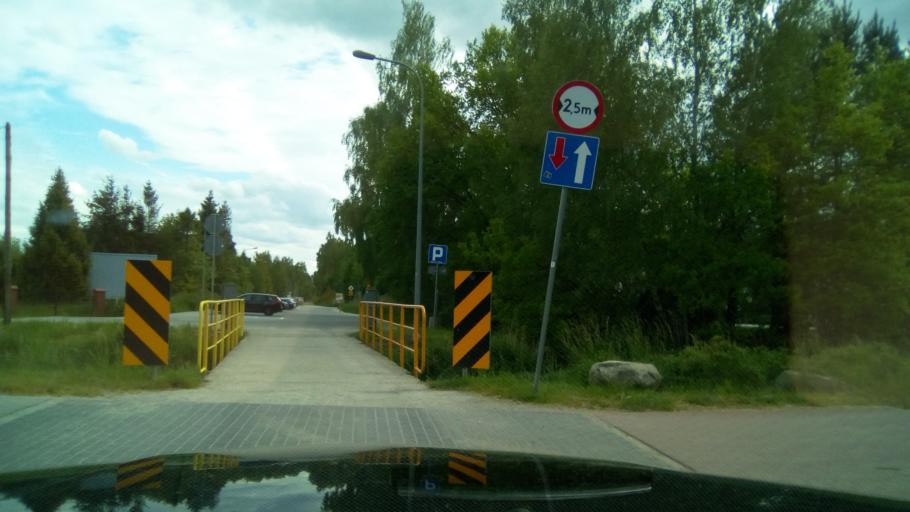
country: PL
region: Pomeranian Voivodeship
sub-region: Powiat pucki
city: Wierzchucino
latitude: 54.8274
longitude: 18.0763
